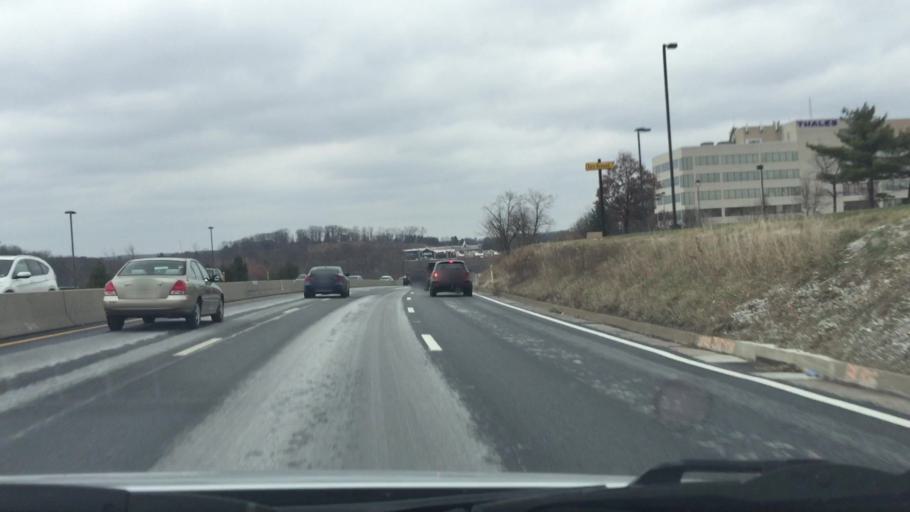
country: US
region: Pennsylvania
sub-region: Allegheny County
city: West View
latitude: 40.5623
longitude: -80.0252
